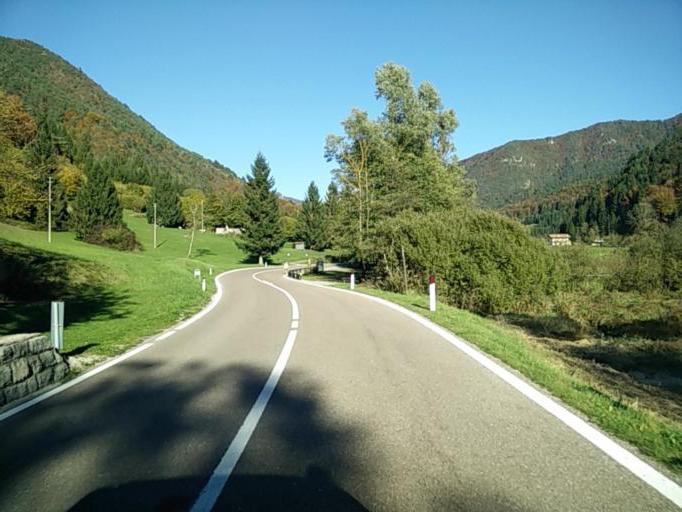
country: IT
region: Trentino-Alto Adige
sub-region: Provincia di Trento
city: Cimego
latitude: 45.8729
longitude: 10.6532
